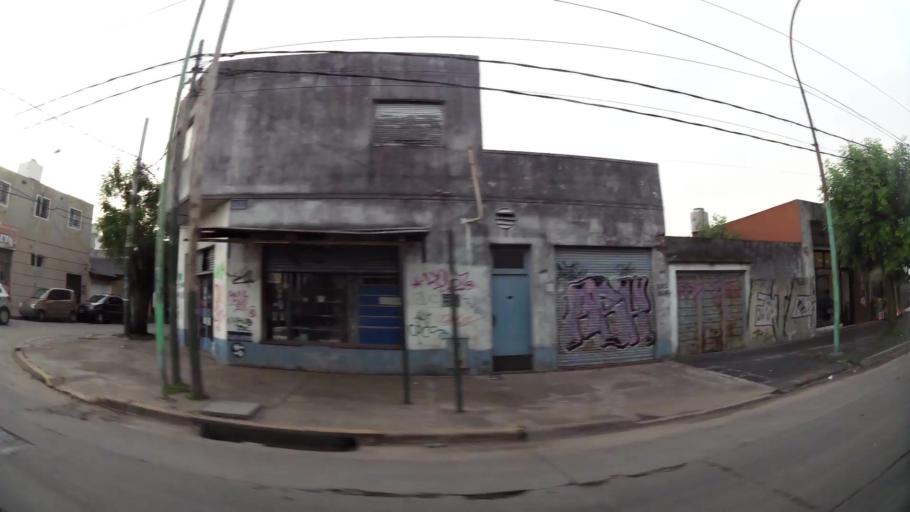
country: AR
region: Buenos Aires
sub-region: Partido de Lomas de Zamora
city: Lomas de Zamora
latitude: -34.7740
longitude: -58.3858
